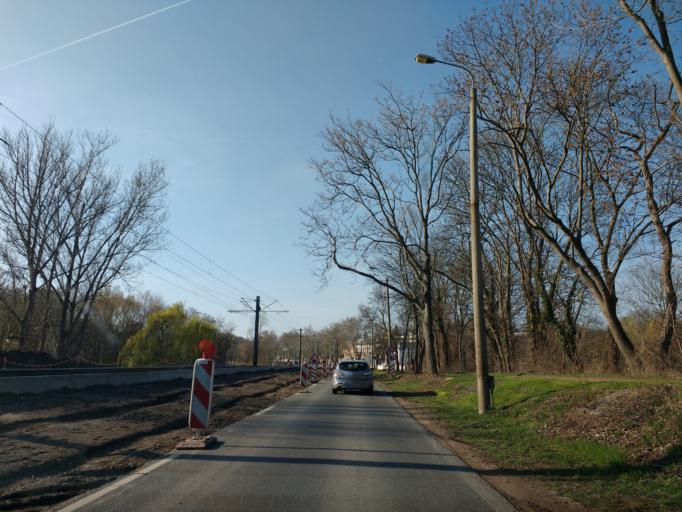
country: DE
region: Saxony-Anhalt
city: Halle Neustadt
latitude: 51.4926
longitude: 11.9431
